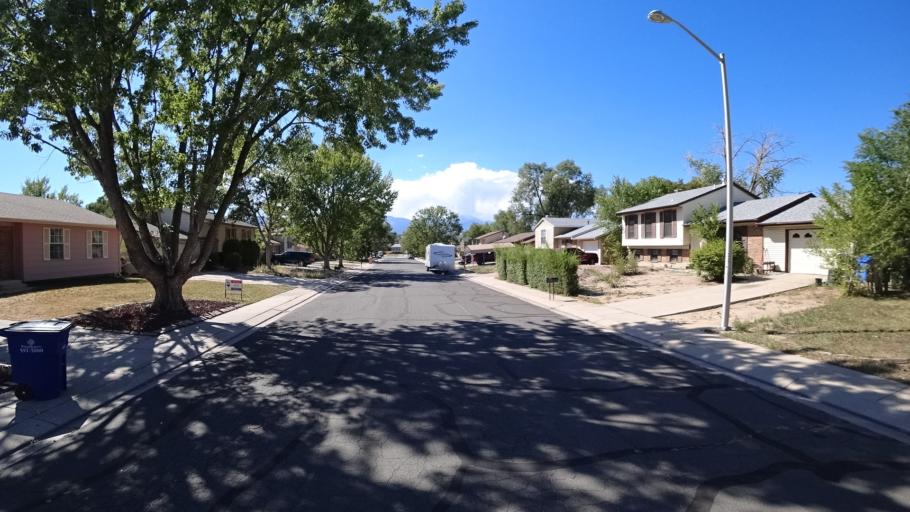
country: US
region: Colorado
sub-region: El Paso County
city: Stratmoor
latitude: 38.7958
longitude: -104.7398
